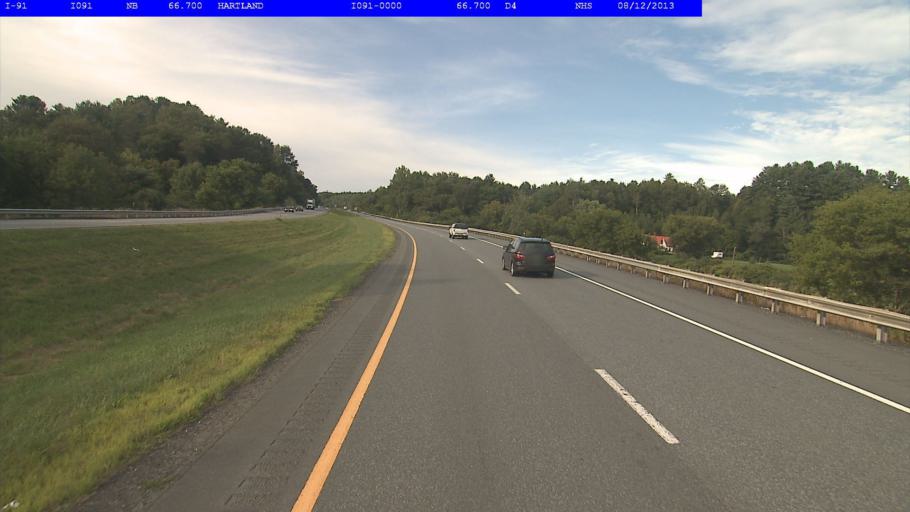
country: US
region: Vermont
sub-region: Windsor County
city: White River Junction
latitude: 43.5972
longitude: -72.3449
